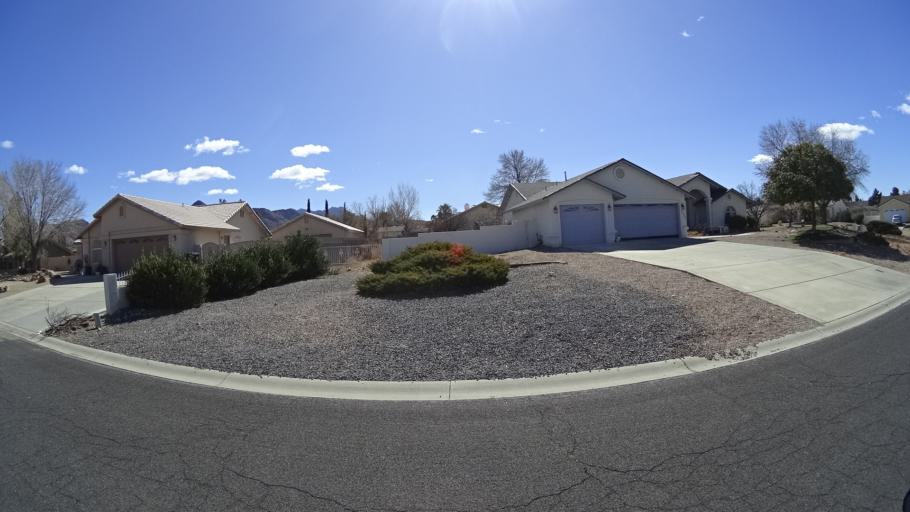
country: US
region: Arizona
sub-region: Mohave County
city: Kingman
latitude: 35.2010
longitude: -113.9633
